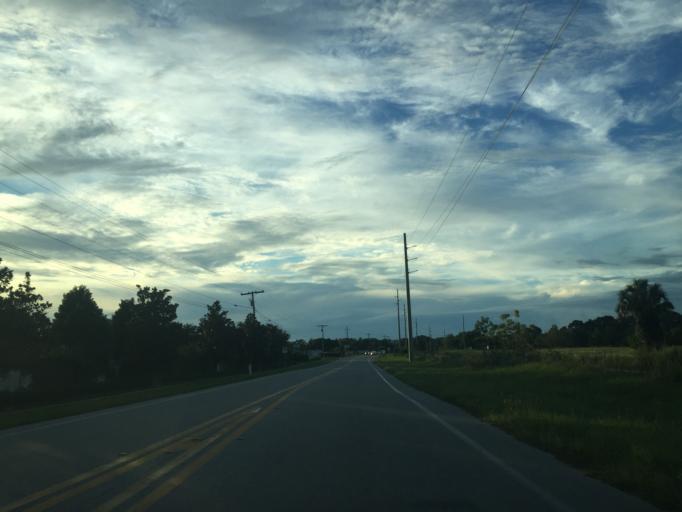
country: US
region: Florida
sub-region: Lake County
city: Tavares
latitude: 28.7776
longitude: -81.7445
